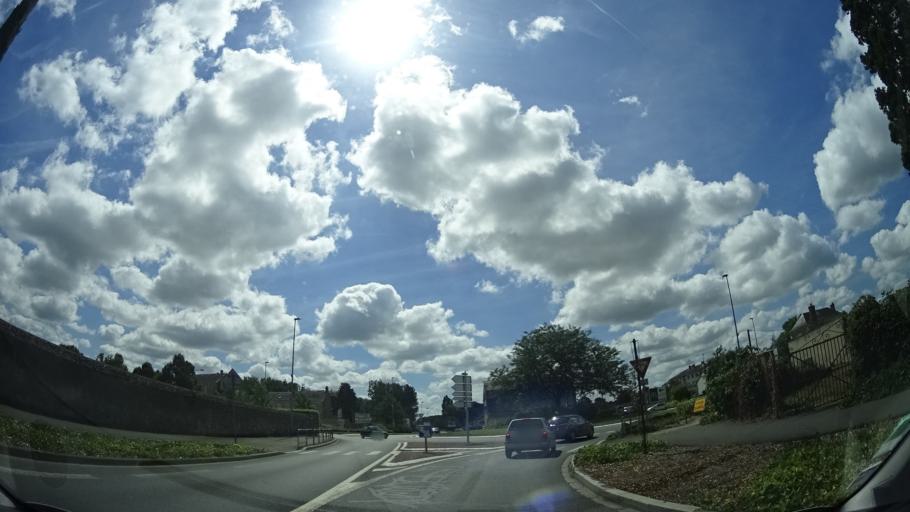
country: FR
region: Pays de la Loire
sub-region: Departement de la Sarthe
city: La Fleche
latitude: 47.6987
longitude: -0.0880
